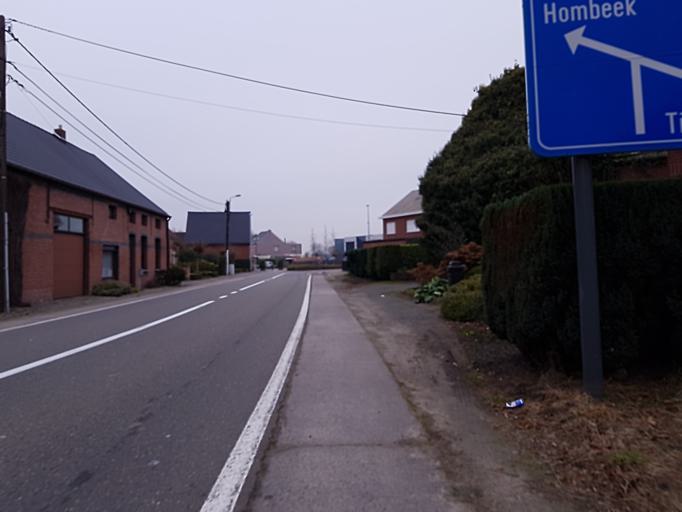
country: BE
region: Flanders
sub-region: Provincie Vlaams-Brabant
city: Kapelle-op-den-Bos
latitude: 51.0324
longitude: 4.3946
